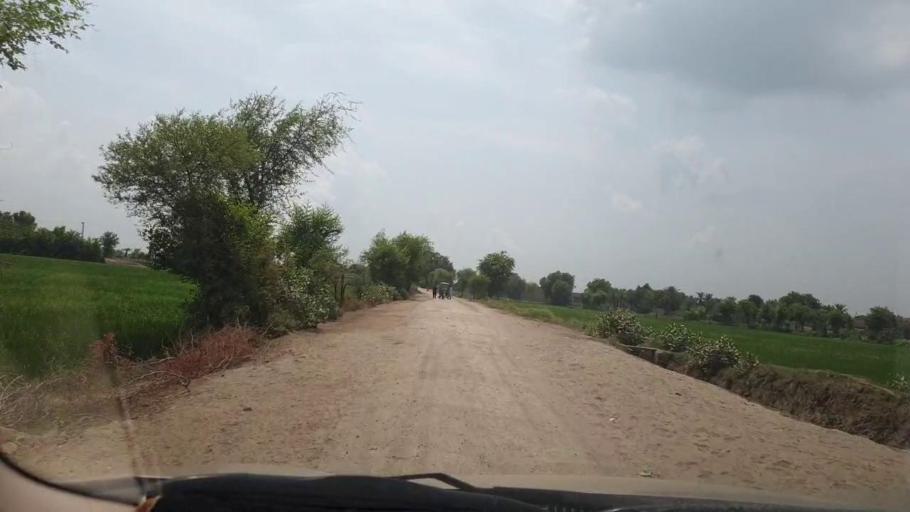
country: PK
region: Sindh
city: Larkana
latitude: 27.6059
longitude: 68.1263
